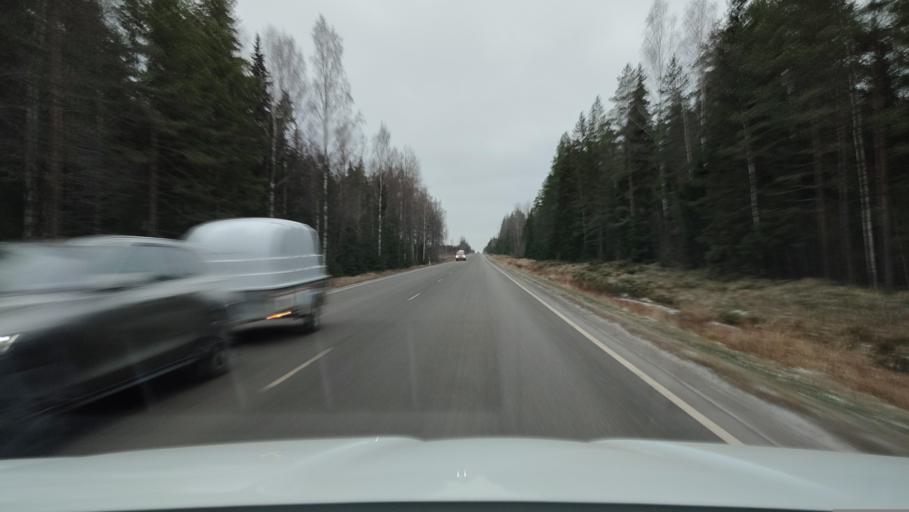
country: FI
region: Ostrobothnia
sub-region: Sydosterbotten
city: Naerpes
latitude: 62.4937
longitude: 21.4454
